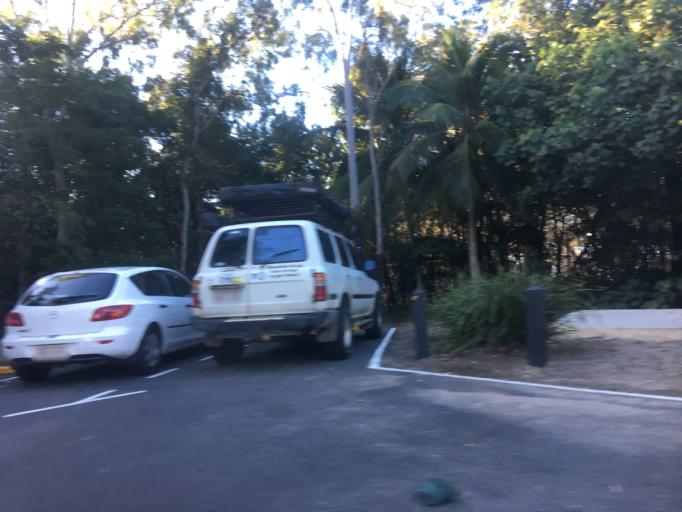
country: AU
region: Queensland
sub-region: Cairns
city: Yorkeys Knob
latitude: -16.7983
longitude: 145.7101
